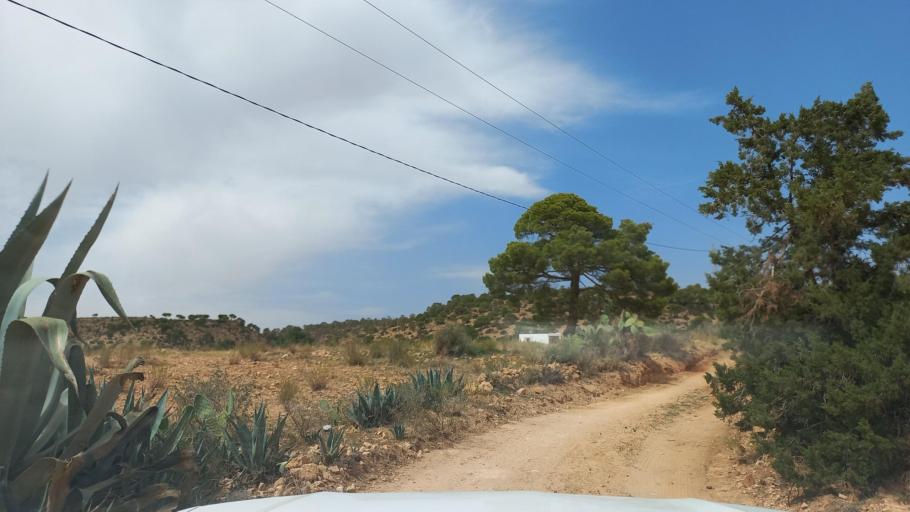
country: TN
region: Al Qasrayn
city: Kasserine
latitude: 35.3725
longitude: 8.8912
